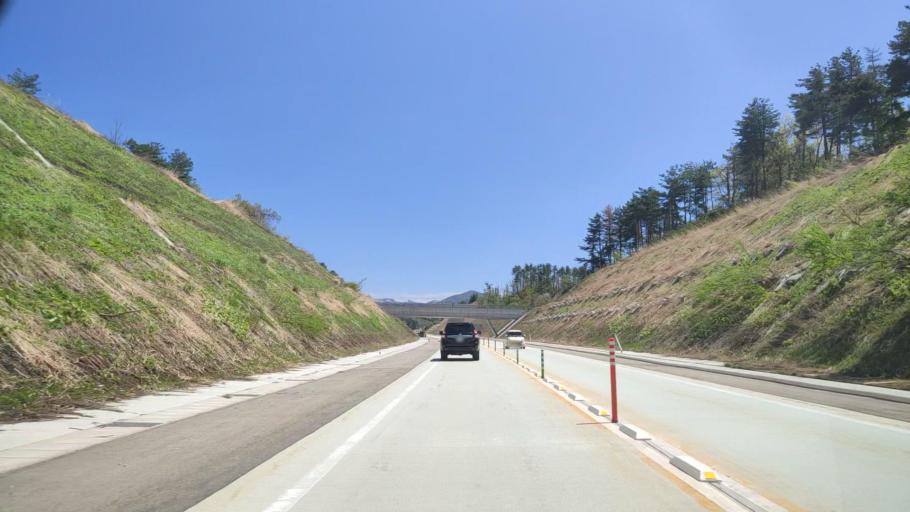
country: JP
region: Yamagata
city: Obanazawa
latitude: 38.5886
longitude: 140.3903
